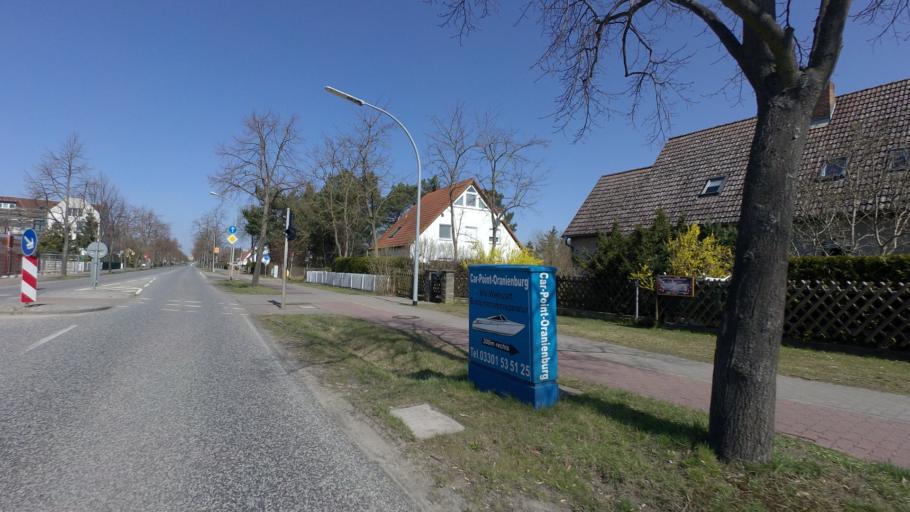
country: DE
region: Brandenburg
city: Oranienburg
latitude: 52.7366
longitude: 13.2423
